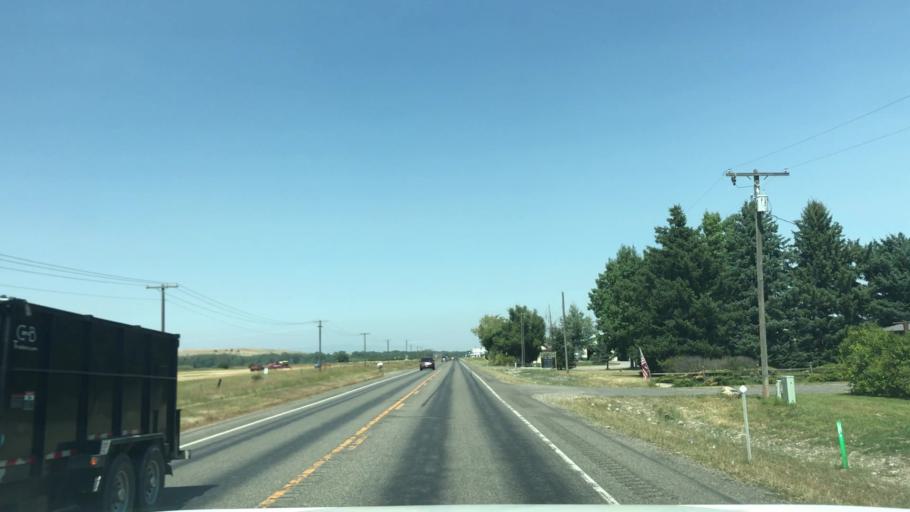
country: US
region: Montana
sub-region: Gallatin County
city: Four Corners
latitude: 45.6261
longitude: -111.1969
